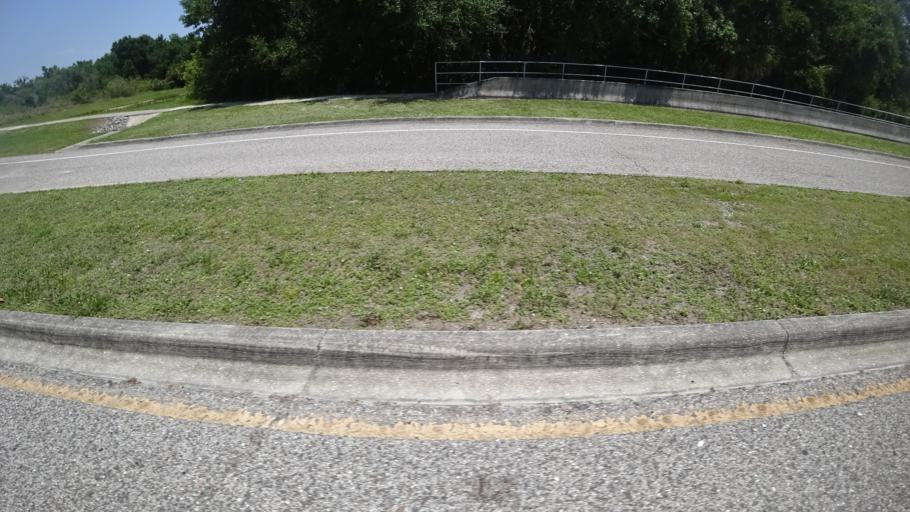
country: US
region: Florida
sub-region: Sarasota County
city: Desoto Lakes
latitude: 27.4121
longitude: -82.4653
